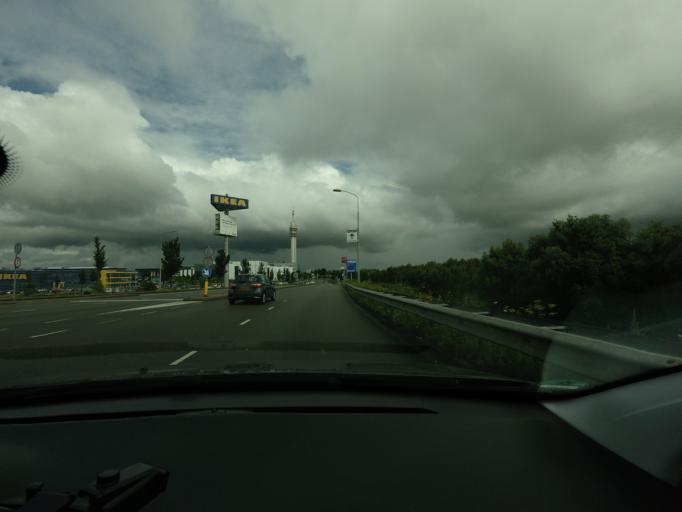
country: NL
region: North Holland
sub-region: Gemeente Haarlem
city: Haarlem
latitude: 52.3836
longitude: 4.6737
